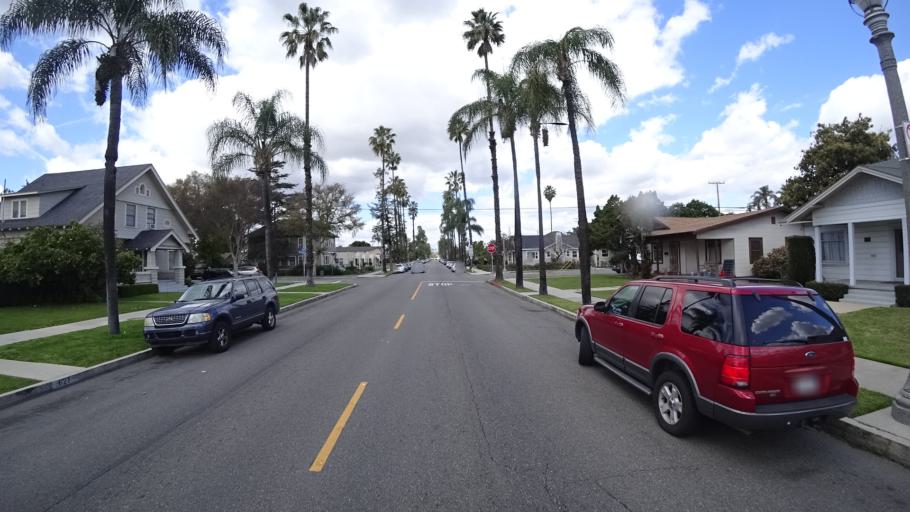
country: US
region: California
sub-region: Orange County
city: Anaheim
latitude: 33.8412
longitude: -117.9179
